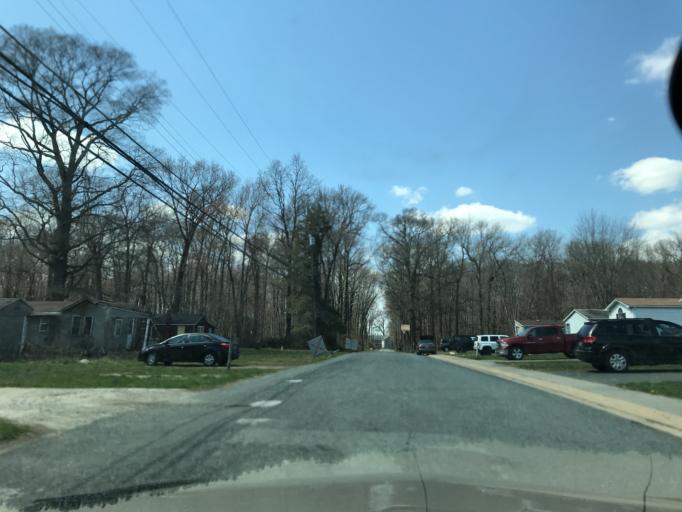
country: US
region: Maryland
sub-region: Harford County
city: Riverside
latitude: 39.4486
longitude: -76.2277
